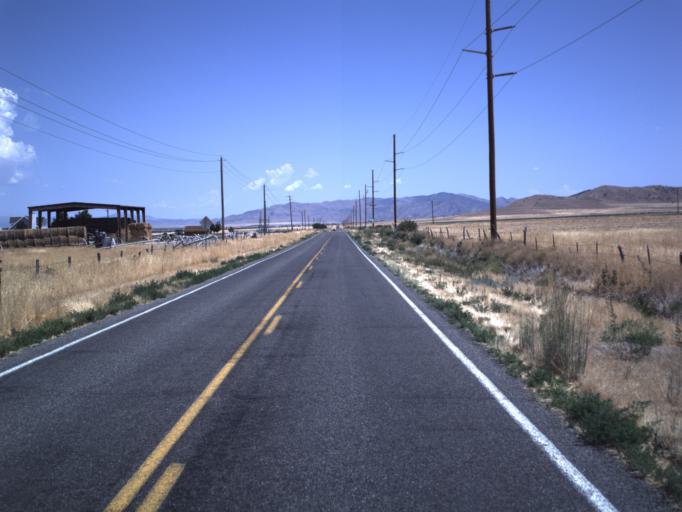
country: US
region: Utah
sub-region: Millard County
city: Delta
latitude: 39.4002
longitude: -112.3351
